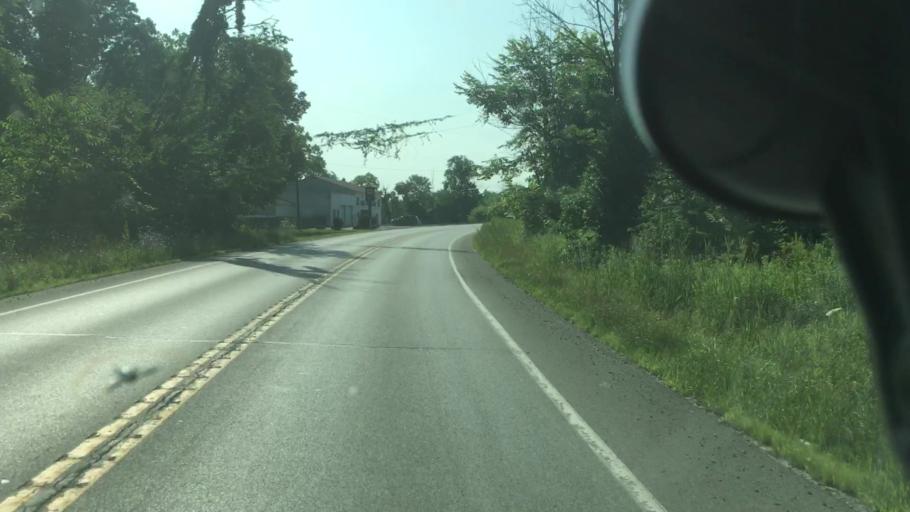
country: US
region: Ohio
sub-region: Mahoning County
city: Lowellville
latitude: 41.0210
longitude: -80.5027
